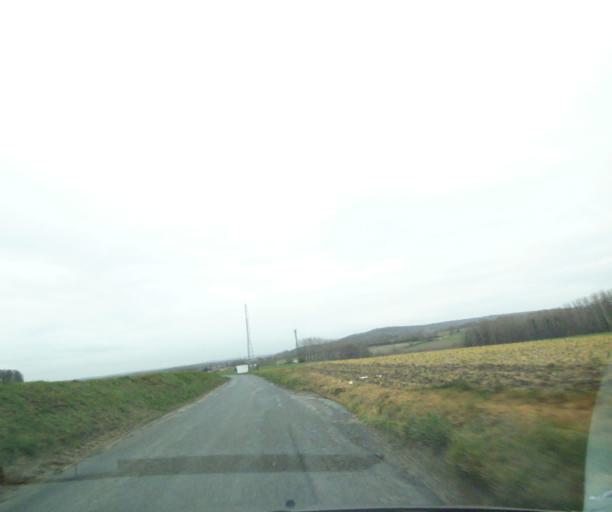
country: FR
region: Picardie
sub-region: Departement de l'Oise
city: Noyon
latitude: 49.5689
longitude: 2.9701
